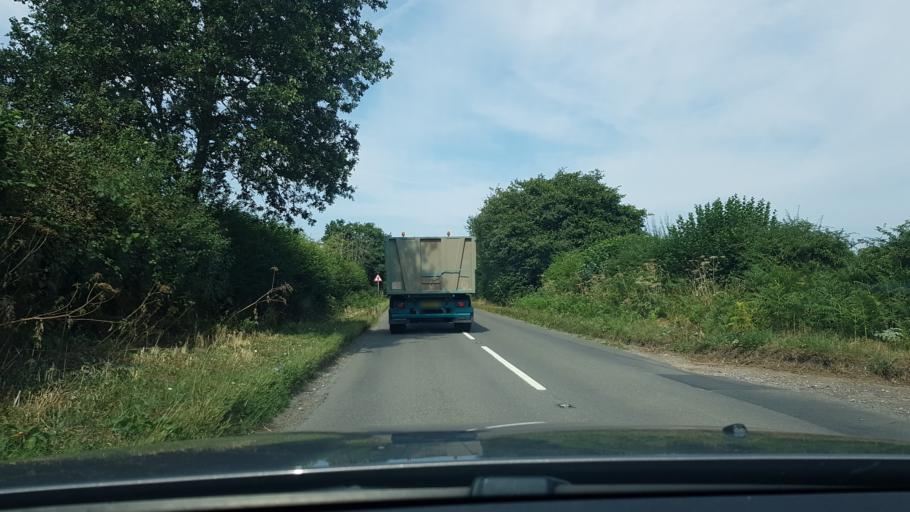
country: GB
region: England
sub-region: West Berkshire
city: Lambourn
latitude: 51.4867
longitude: -1.5474
